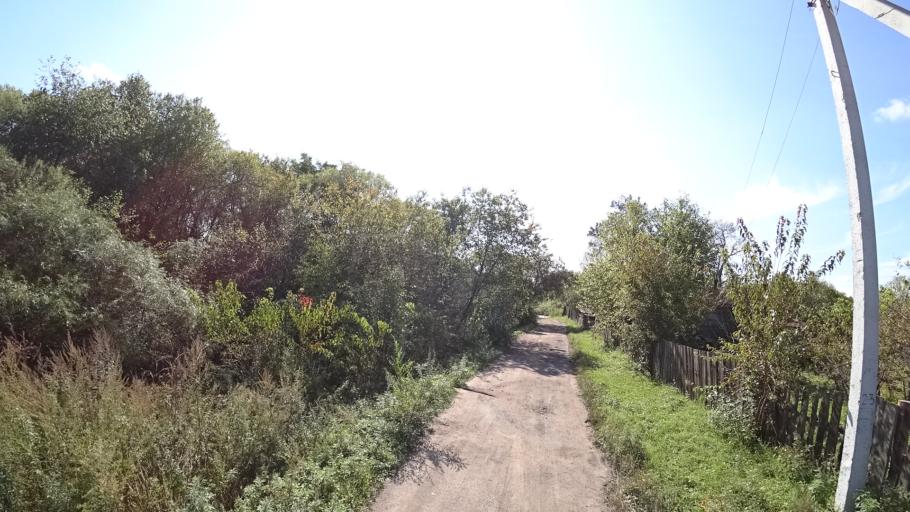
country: RU
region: Amur
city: Arkhara
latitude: 49.4006
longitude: 130.1322
